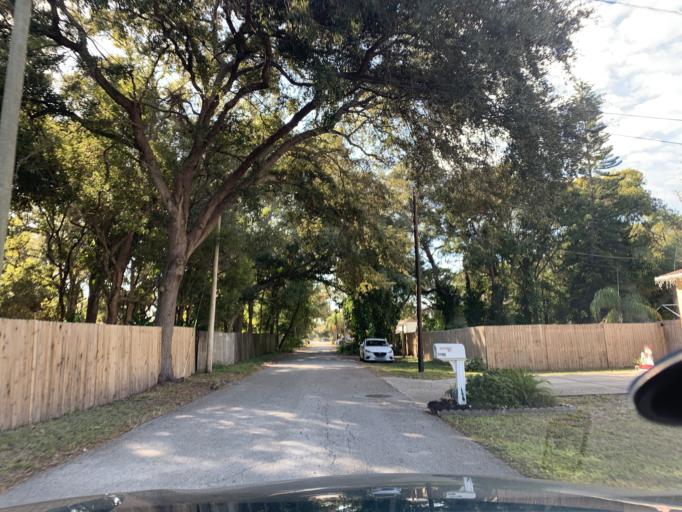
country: US
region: Florida
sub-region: Pinellas County
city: Kenneth City
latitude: 27.8155
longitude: -82.7358
